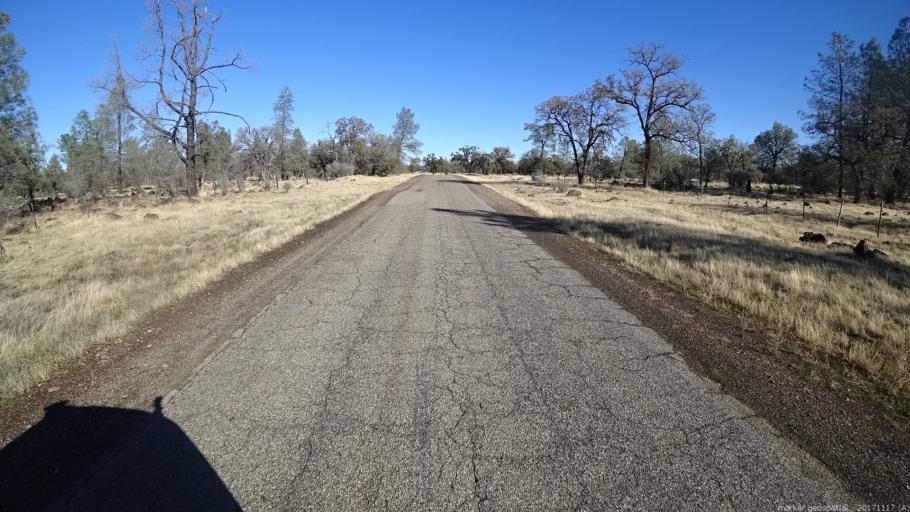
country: US
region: California
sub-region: Shasta County
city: Palo Cedro
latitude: 40.4513
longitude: -122.1109
